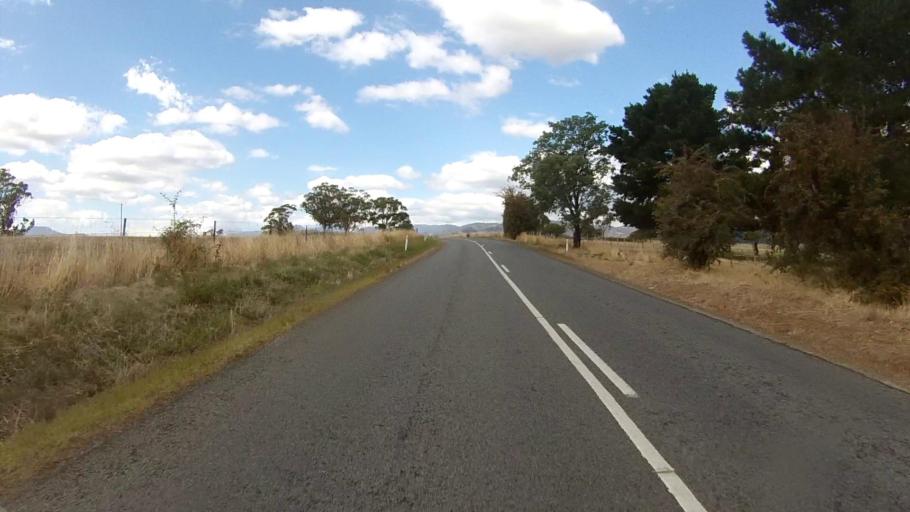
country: AU
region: Tasmania
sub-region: Derwent Valley
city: New Norfolk
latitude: -42.7513
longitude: 146.9756
